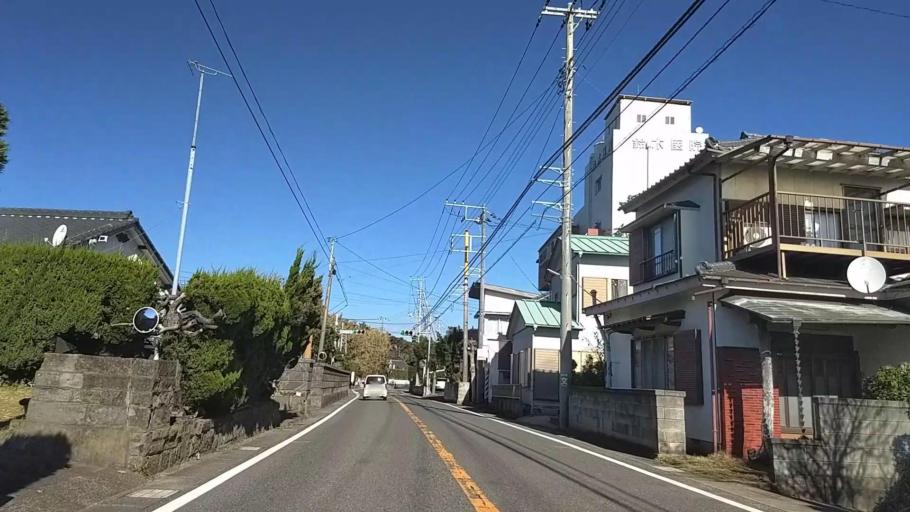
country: JP
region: Chiba
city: Tateyama
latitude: 34.9912
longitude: 139.9671
